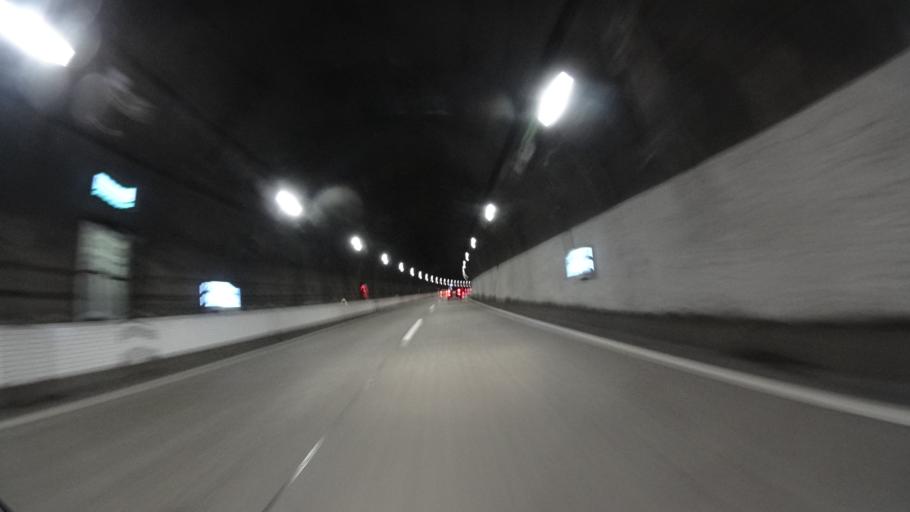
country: JP
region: Nagano
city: Nagano-shi
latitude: 36.5589
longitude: 138.1662
